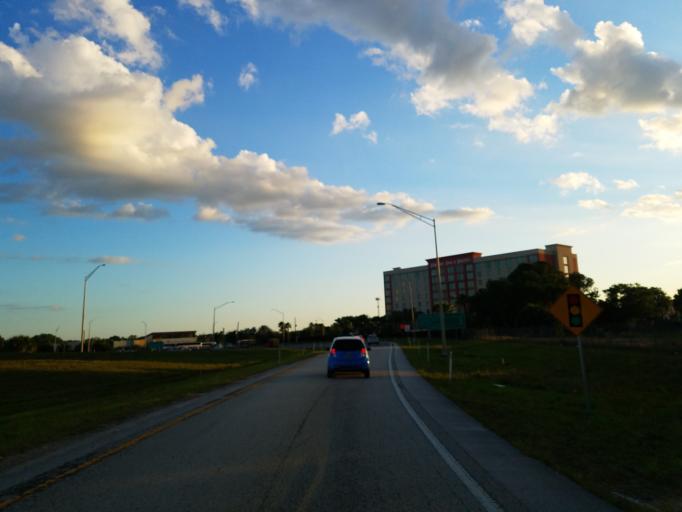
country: US
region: Florida
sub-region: Orange County
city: Doctor Phillips
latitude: 28.4523
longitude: -81.4752
